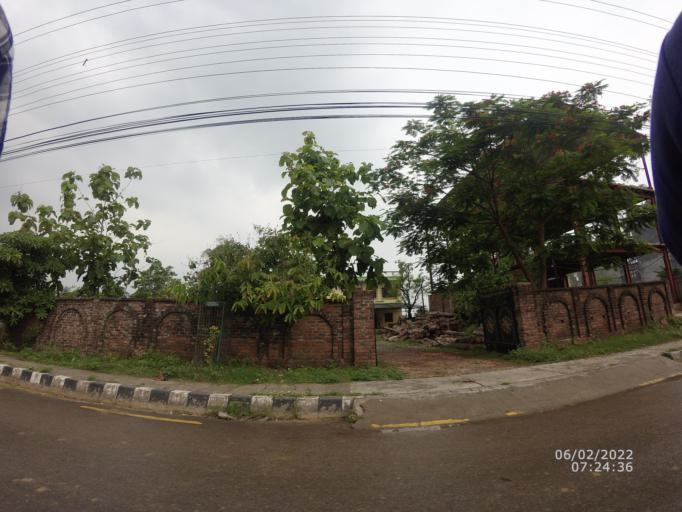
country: NP
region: Western Region
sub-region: Lumbini Zone
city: Bhairahawa
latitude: 27.4989
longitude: 83.4480
